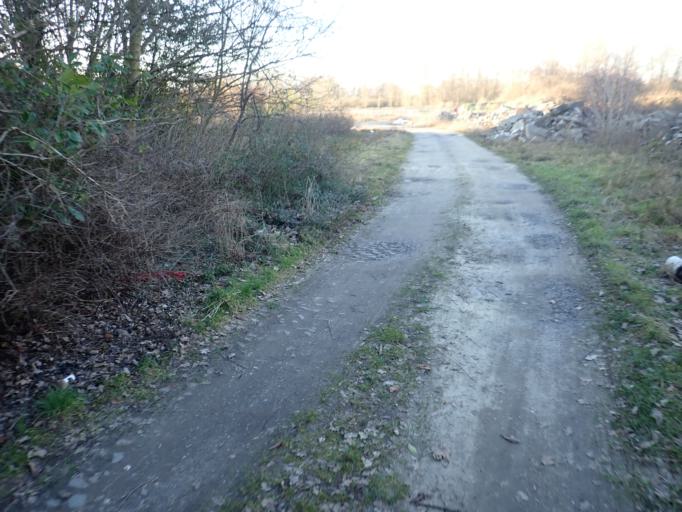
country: BE
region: Flanders
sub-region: Provincie Oost-Vlaanderen
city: Buggenhout
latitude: 51.0309
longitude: 4.1873
